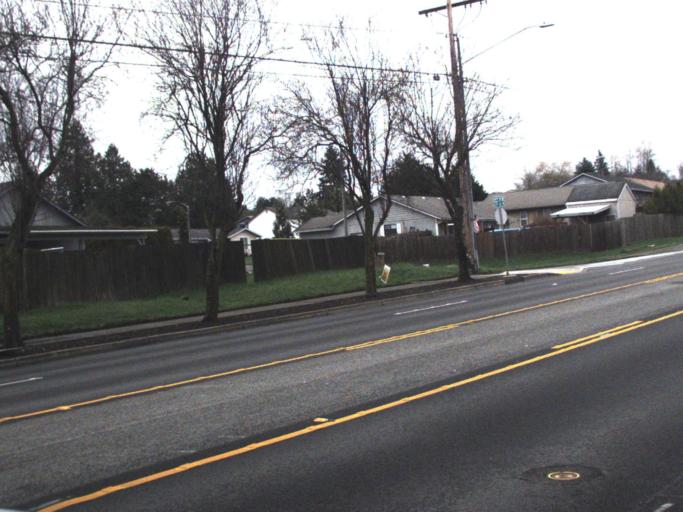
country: US
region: Washington
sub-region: Snohomish County
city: Marysville
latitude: 48.0537
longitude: -122.1434
